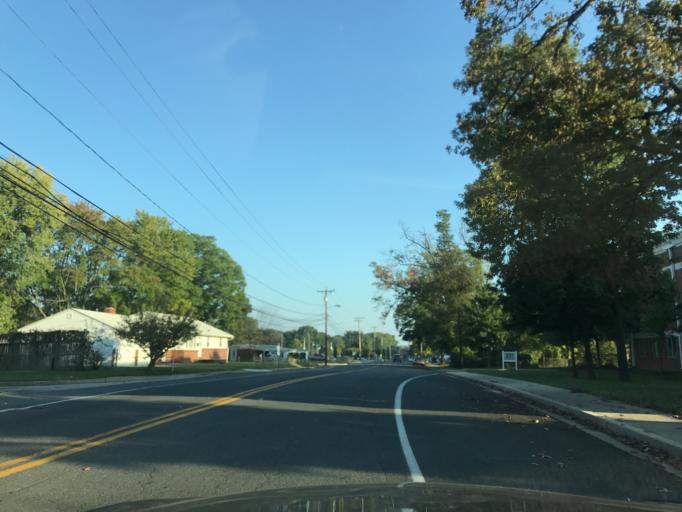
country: US
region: Maryland
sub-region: Anne Arundel County
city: South Gate
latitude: 39.1455
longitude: -76.6307
